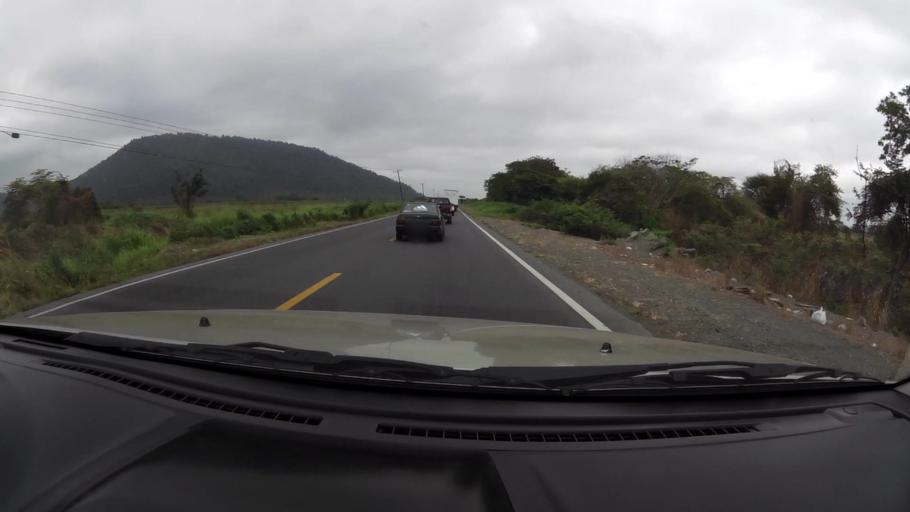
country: EC
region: Guayas
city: Naranjal
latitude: -2.4295
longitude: -79.6258
